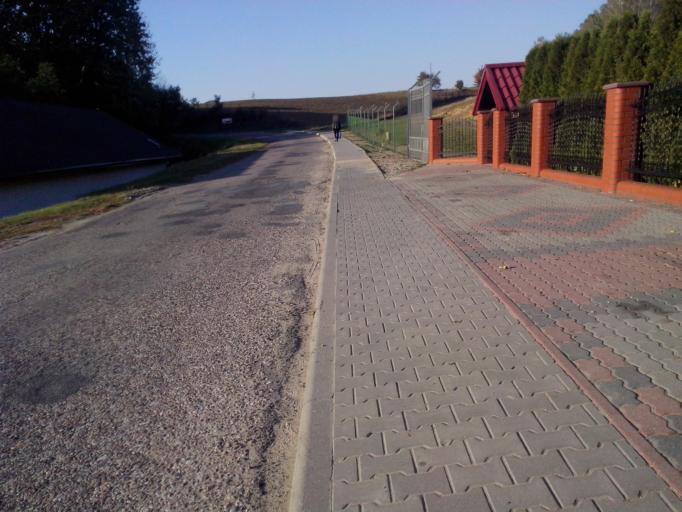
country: PL
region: Kujawsko-Pomorskie
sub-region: Powiat brodnicki
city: Brzozie
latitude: 53.2864
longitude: 19.6945
